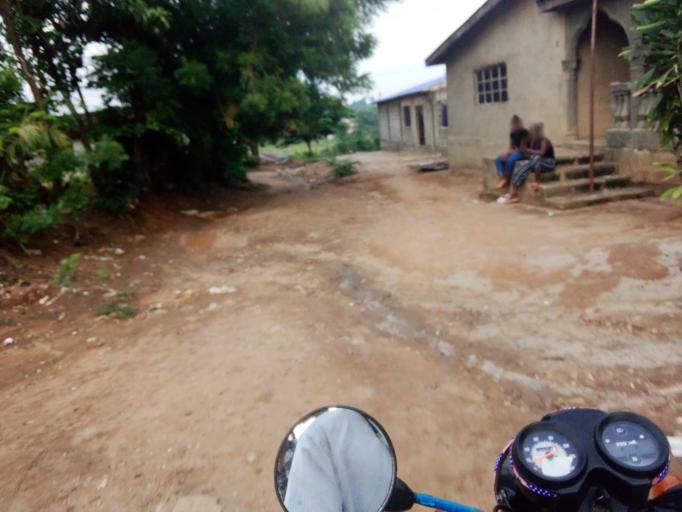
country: SL
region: Western Area
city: Waterloo
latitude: 8.3321
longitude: -13.0692
